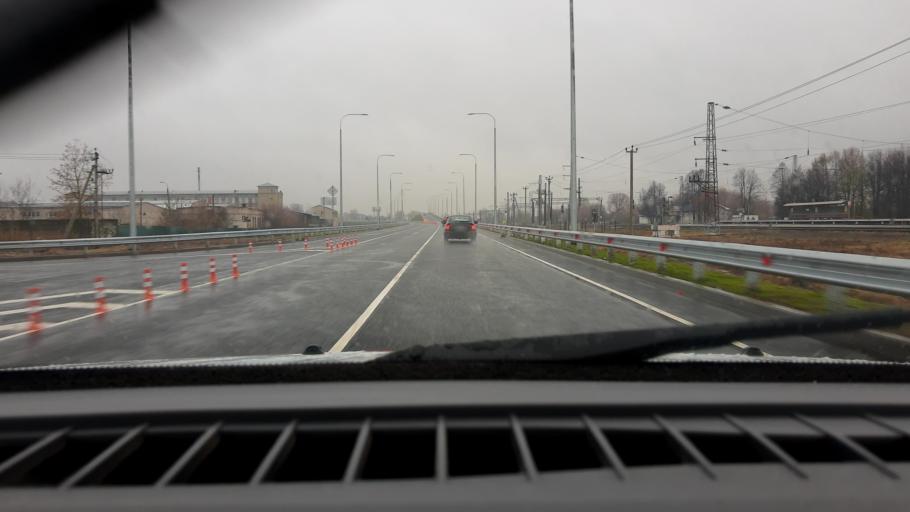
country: RU
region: Nizjnij Novgorod
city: Neklyudovo
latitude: 56.4077
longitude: 43.9832
